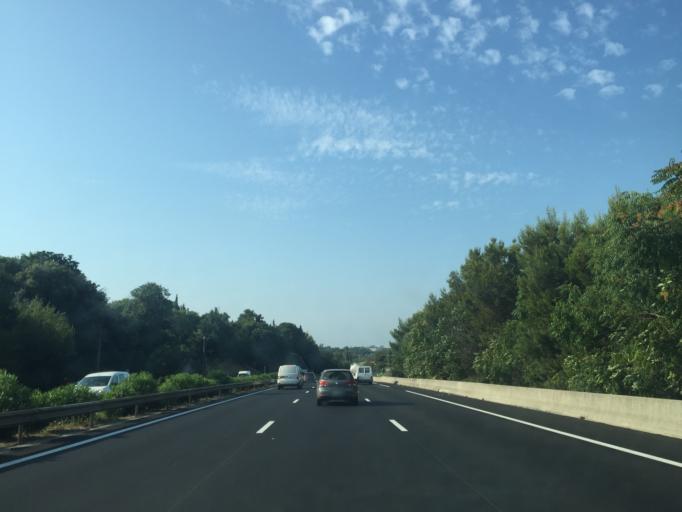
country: FR
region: Provence-Alpes-Cote d'Azur
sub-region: Departement des Alpes-Maritimes
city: Biot
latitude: 43.6208
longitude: 7.1159
